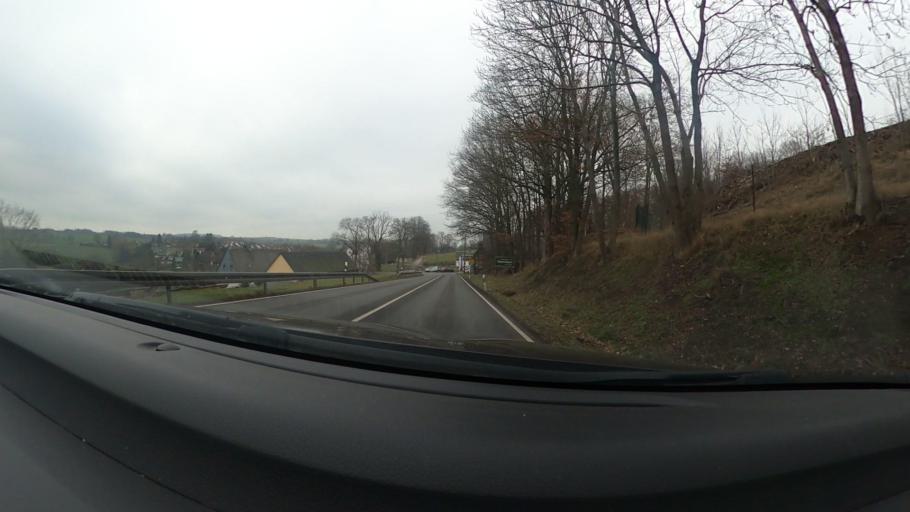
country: DE
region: Saxony
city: Oberschona
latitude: 50.9001
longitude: 13.2521
